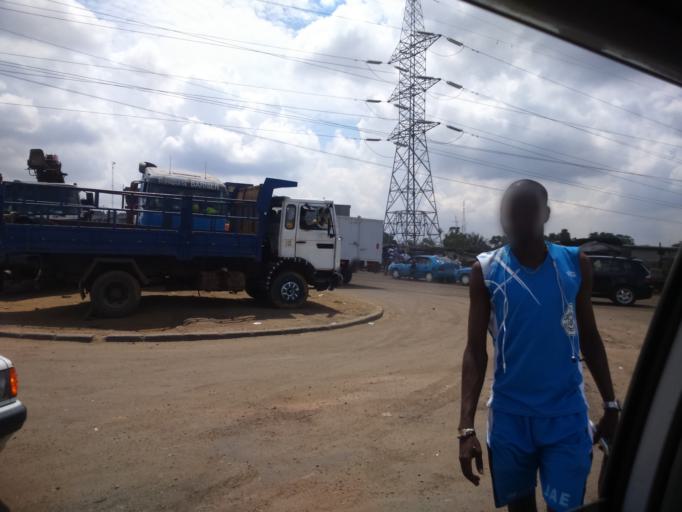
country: CI
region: Lagunes
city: Abidjan
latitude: 5.3554
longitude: -4.0850
